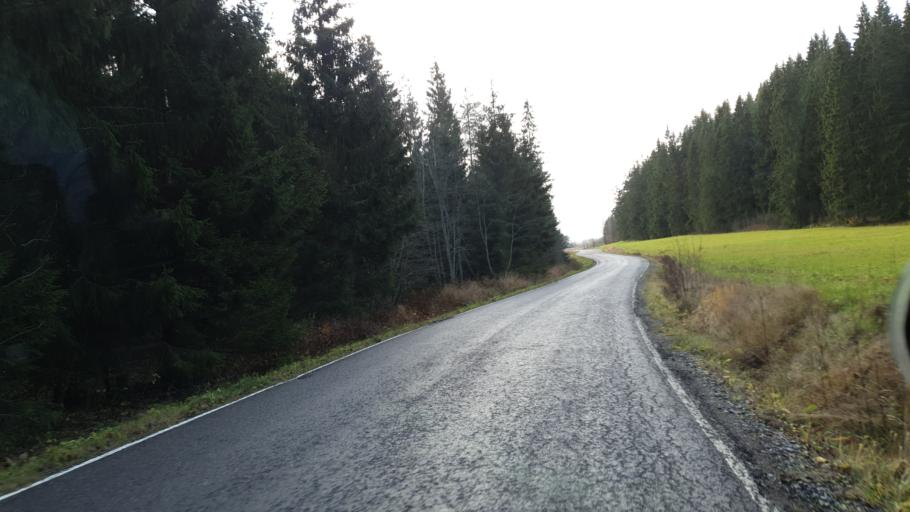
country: FI
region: Uusimaa
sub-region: Helsinki
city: Siuntio
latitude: 60.2632
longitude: 24.3026
